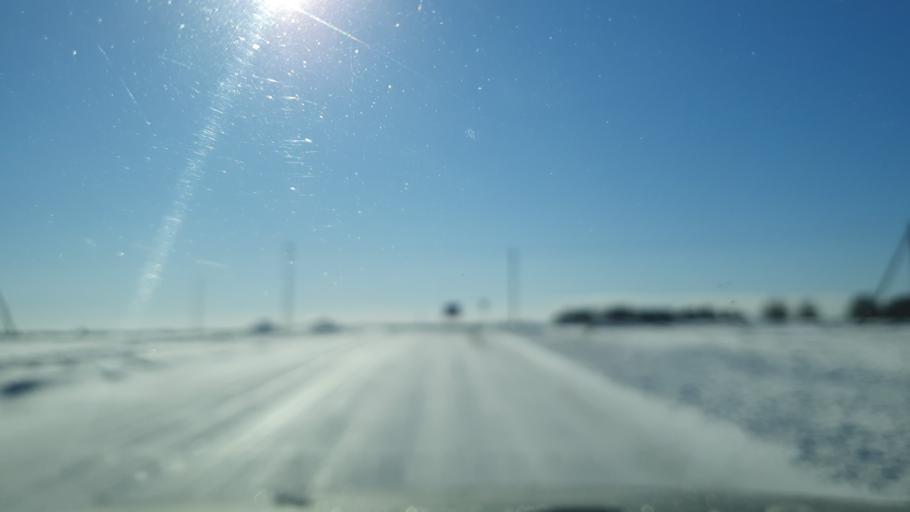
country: EE
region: Laeaene-Virumaa
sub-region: Haljala vald
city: Haljala
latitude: 59.5488
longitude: 26.1344
